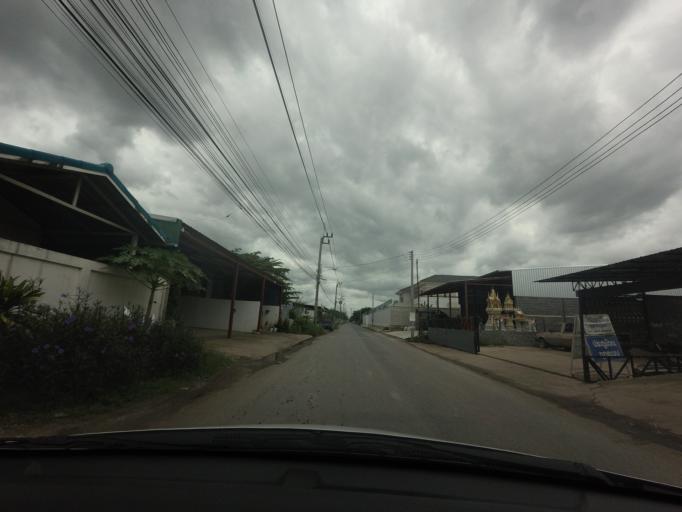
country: TH
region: Bangkok
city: Lat Krabang
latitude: 13.7755
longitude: 100.7735
